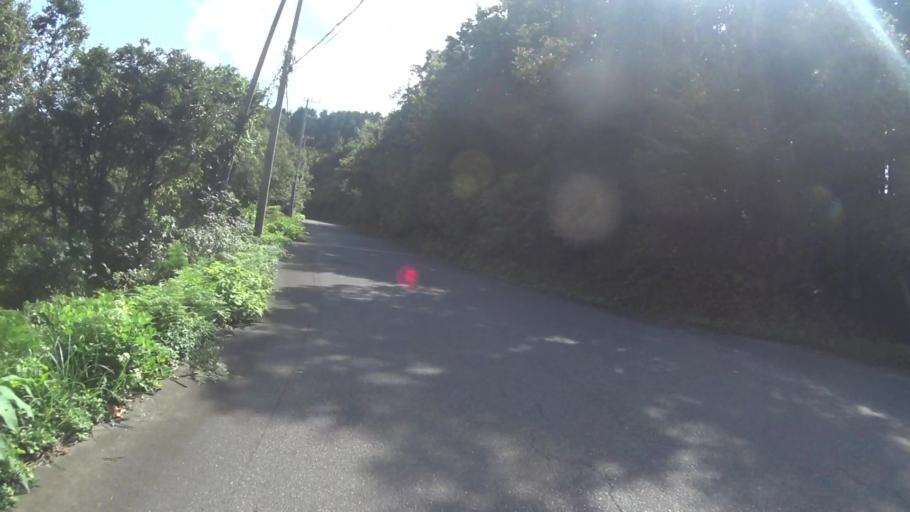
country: JP
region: Kyoto
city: Miyazu
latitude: 35.7090
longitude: 135.1895
